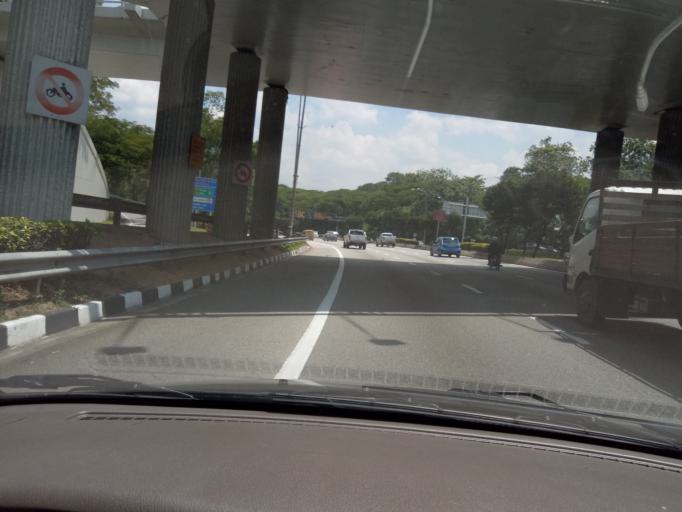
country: MY
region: Kuala Lumpur
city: Kuala Lumpur
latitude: 3.1309
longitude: 101.7013
